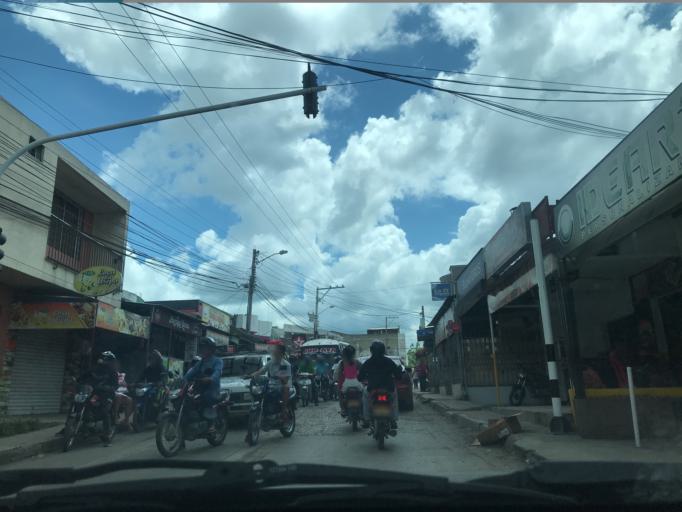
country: CO
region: Sucre
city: Sincelejo
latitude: 9.3096
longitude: -75.3984
